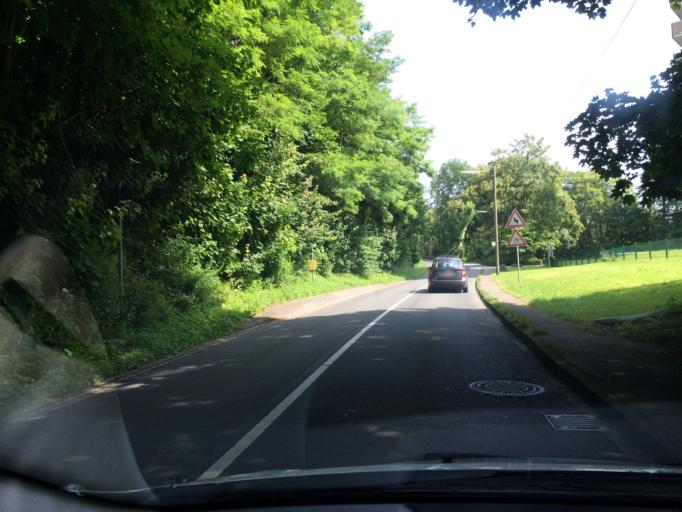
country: DE
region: North Rhine-Westphalia
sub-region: Regierungsbezirk Arnsberg
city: Nachrodt-Wiblingwerde
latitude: 51.3587
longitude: 7.6033
